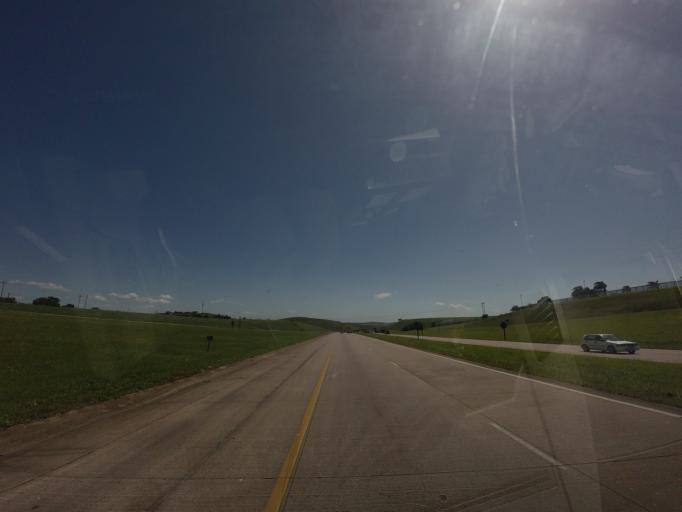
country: ZA
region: KwaZulu-Natal
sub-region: iLembe District Municipality
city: Stanger
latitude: -29.3929
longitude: 31.2925
